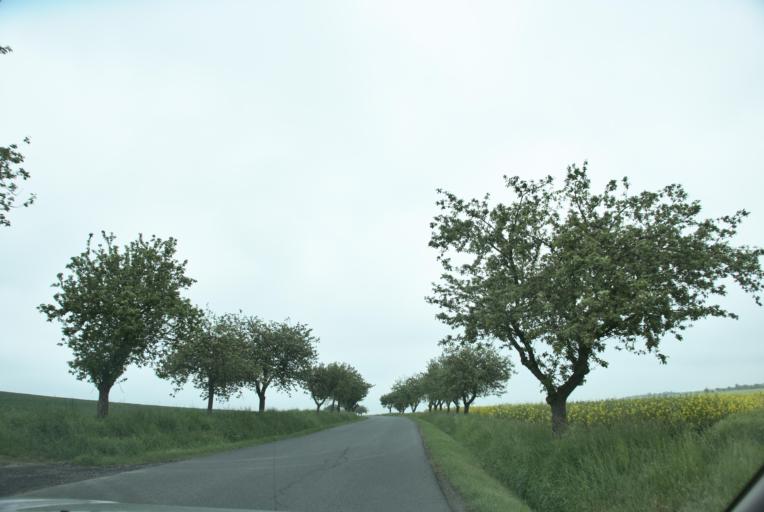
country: CZ
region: Plzensky
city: Zihle
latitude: 50.0077
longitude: 13.4202
